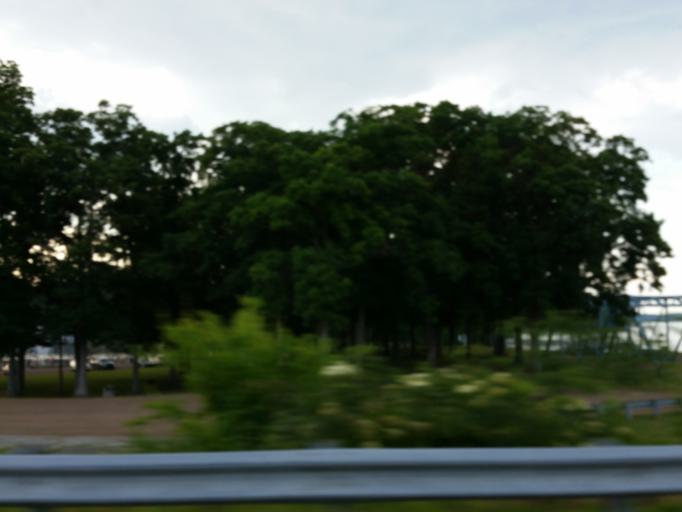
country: US
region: Tennessee
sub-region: Stewart County
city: Dover
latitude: 36.4403
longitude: -88.0780
